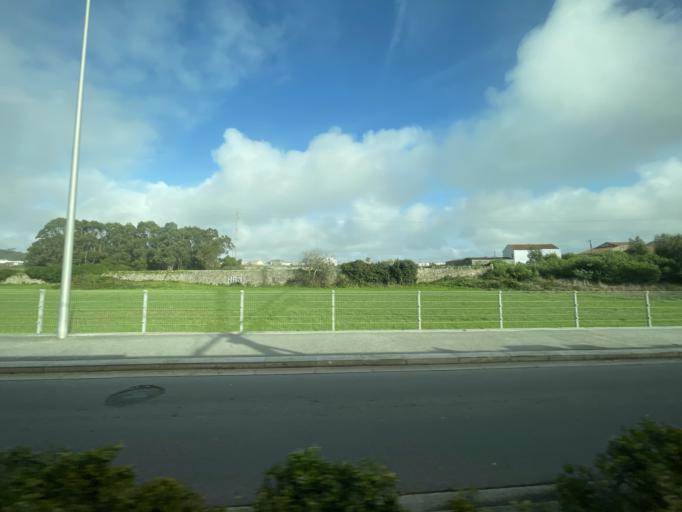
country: PT
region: Porto
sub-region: Vila do Conde
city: Vila do Conde
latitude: 41.3571
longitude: -8.7381
